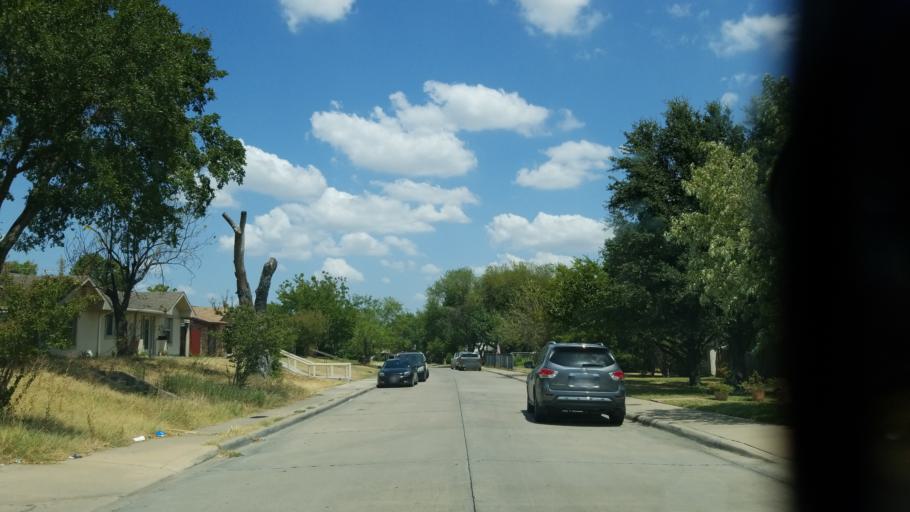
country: US
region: Texas
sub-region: Dallas County
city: Cockrell Hill
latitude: 32.7368
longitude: -96.9218
